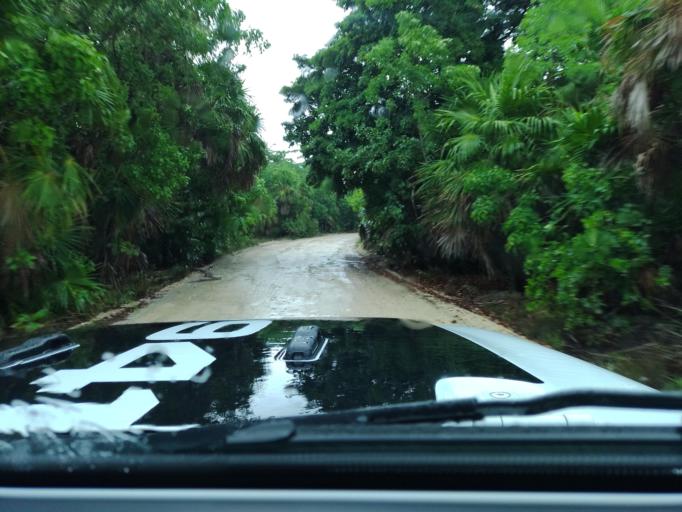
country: MX
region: Quintana Roo
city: Tulum
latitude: 19.9305
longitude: -87.4519
